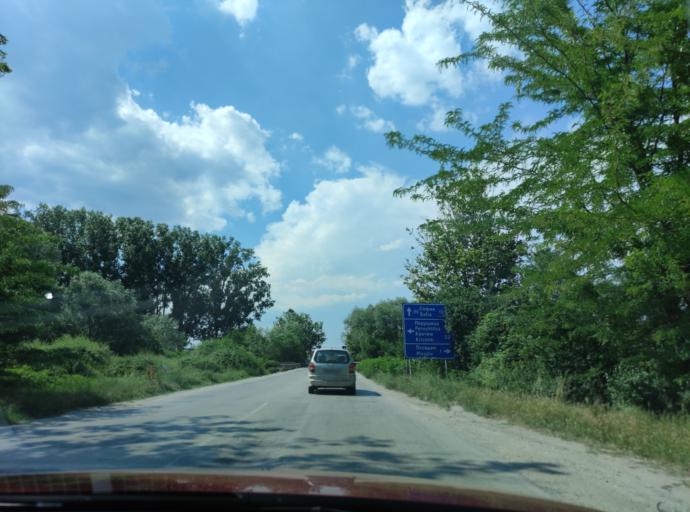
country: BG
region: Plovdiv
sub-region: Obshtina Plovdiv
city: Plovdiv
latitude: 42.1194
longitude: 24.6764
